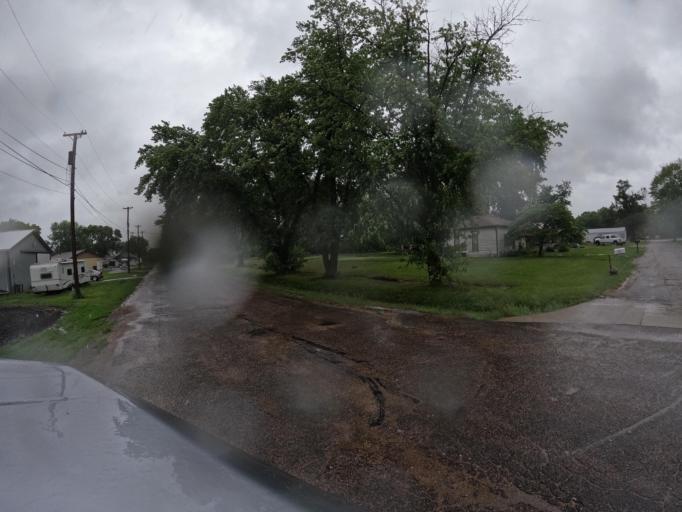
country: US
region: Nebraska
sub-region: Gage County
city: Wymore
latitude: 40.1243
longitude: -96.6558
